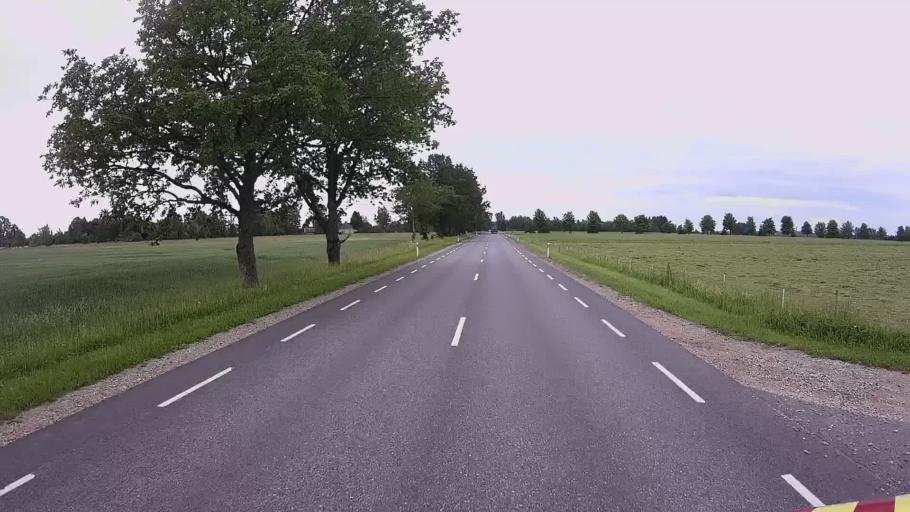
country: EE
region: Viljandimaa
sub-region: Karksi vald
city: Karksi-Nuia
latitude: 58.1282
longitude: 25.5824
